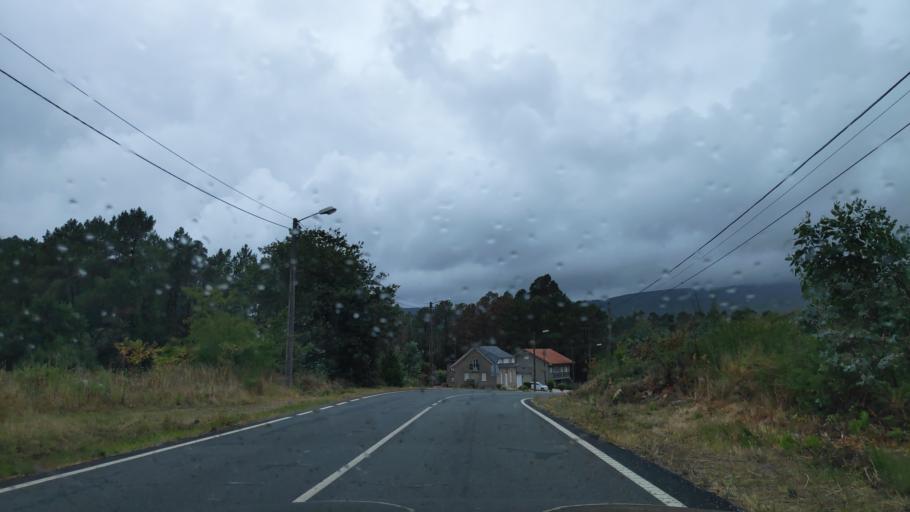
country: ES
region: Galicia
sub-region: Provincia de Pontevedra
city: Catoira
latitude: 42.6926
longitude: -8.7726
